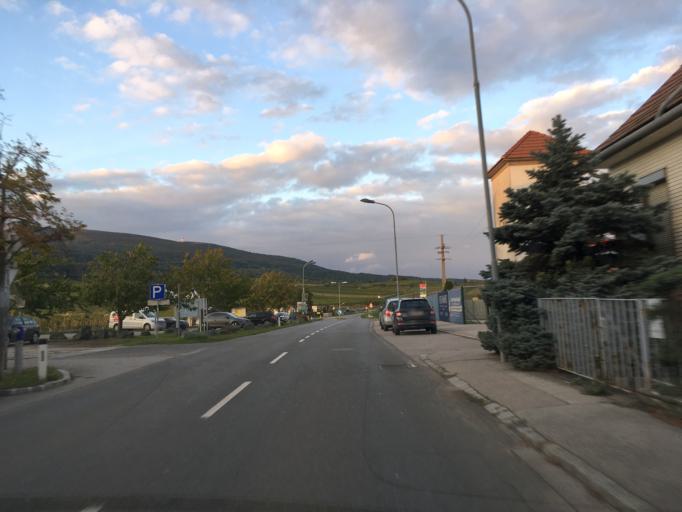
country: AT
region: Lower Austria
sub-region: Politischer Bezirk Baden
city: Pfaffstatten
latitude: 48.0198
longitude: 16.2570
